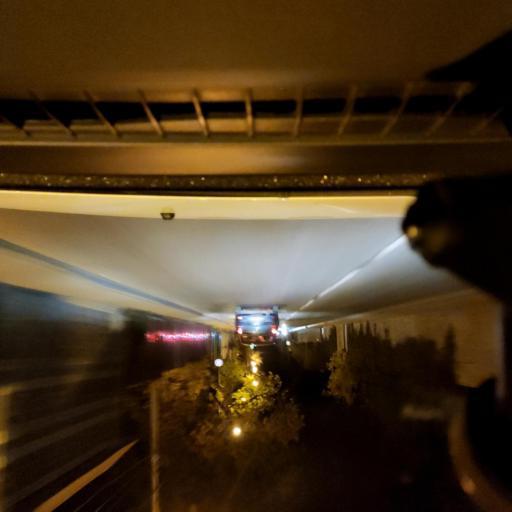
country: RU
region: Samara
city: Samara
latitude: 53.2731
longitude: 50.1924
